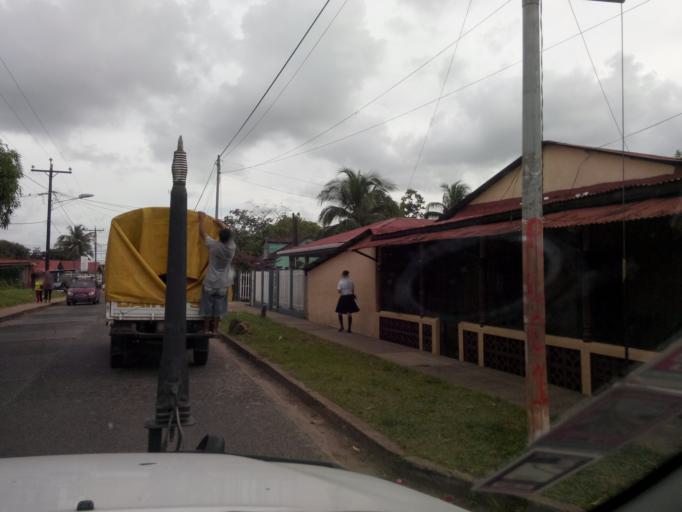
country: NI
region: Atlantico Sur
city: Bluefields
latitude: 12.0159
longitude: -83.7634
